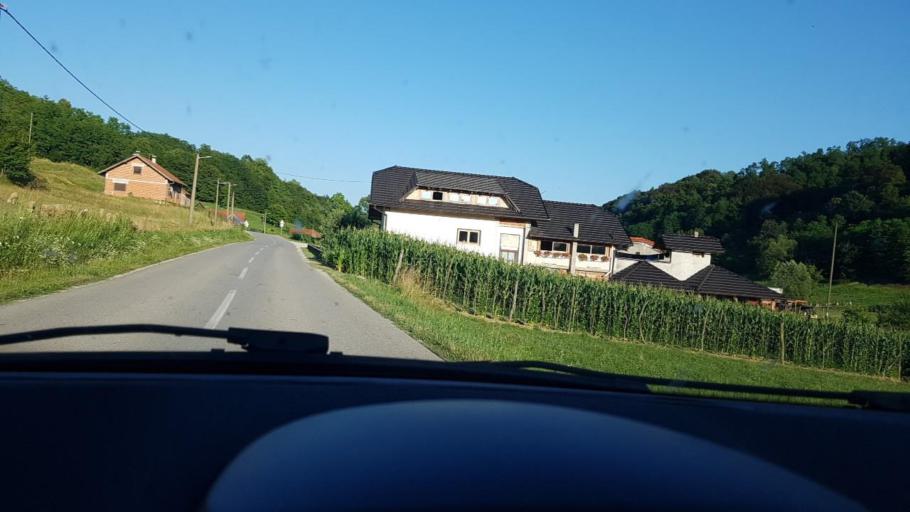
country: HR
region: Krapinsko-Zagorska
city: Bedekovcina
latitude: 46.0702
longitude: 15.9934
